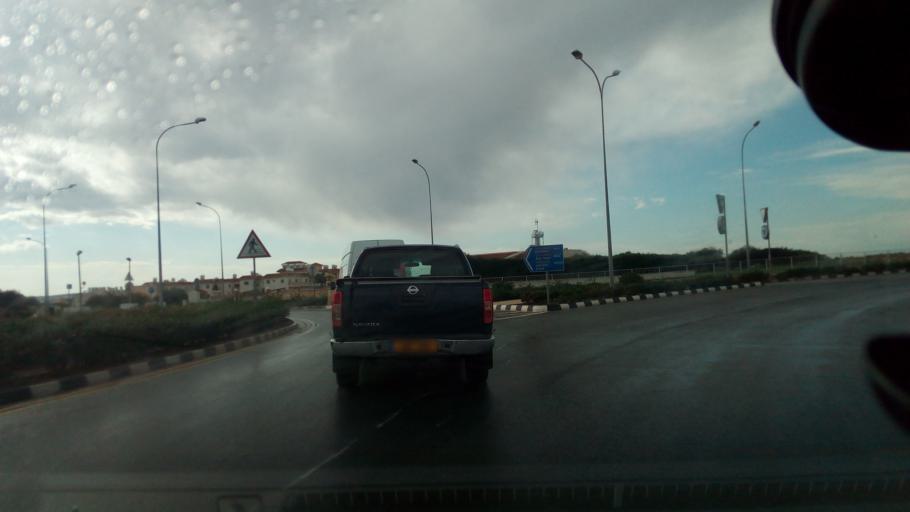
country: CY
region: Ammochostos
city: Paralimni
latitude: 35.0527
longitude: 33.9751
